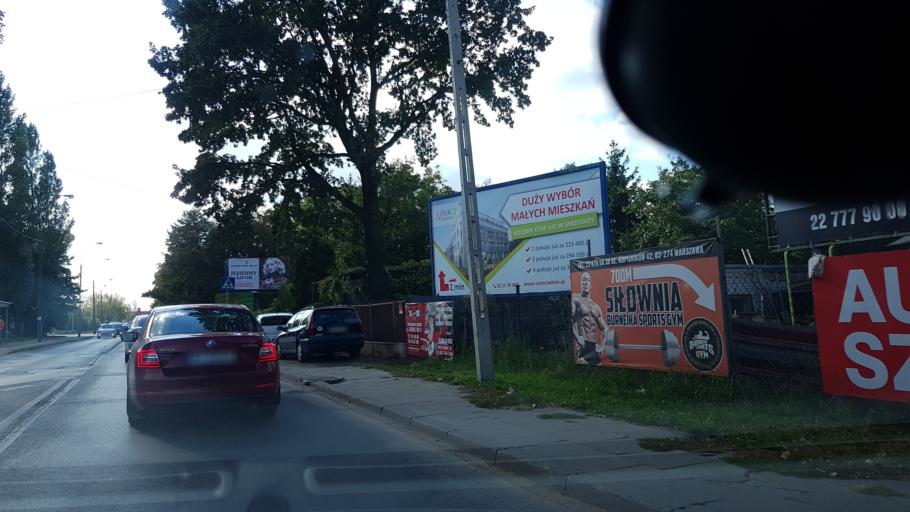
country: PL
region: Masovian Voivodeship
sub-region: Warszawa
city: Targowek
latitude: 52.3009
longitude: 21.0314
